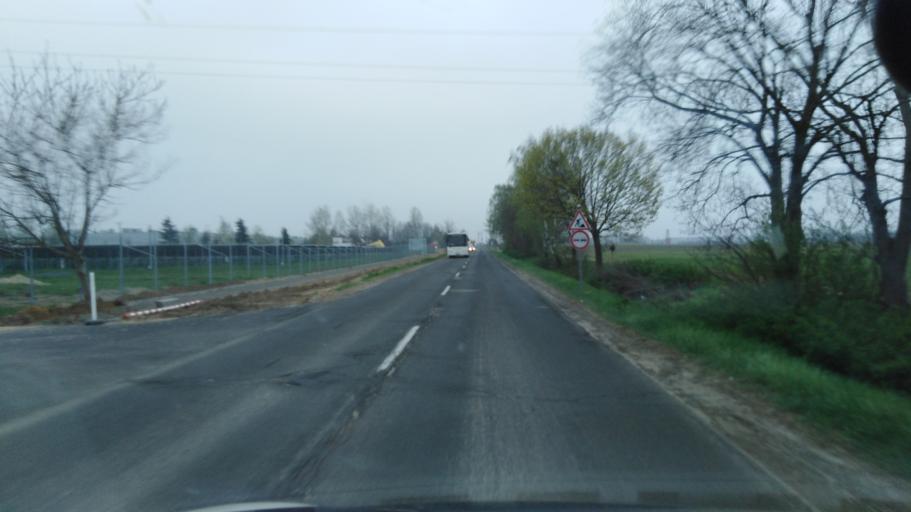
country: HU
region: Nograd
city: Balassagyarmat
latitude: 48.0586
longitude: 19.3070
